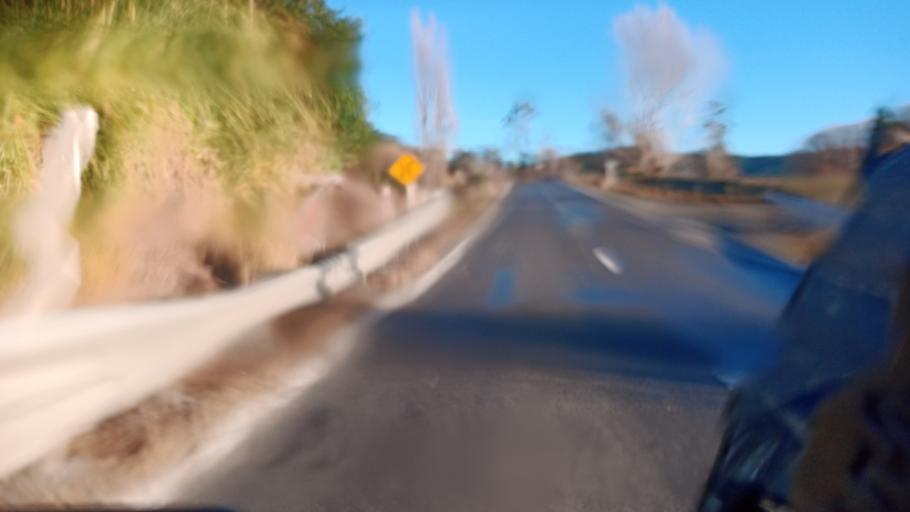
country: NZ
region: Hawke's Bay
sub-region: Wairoa District
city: Wairoa
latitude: -39.0151
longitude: 177.3374
